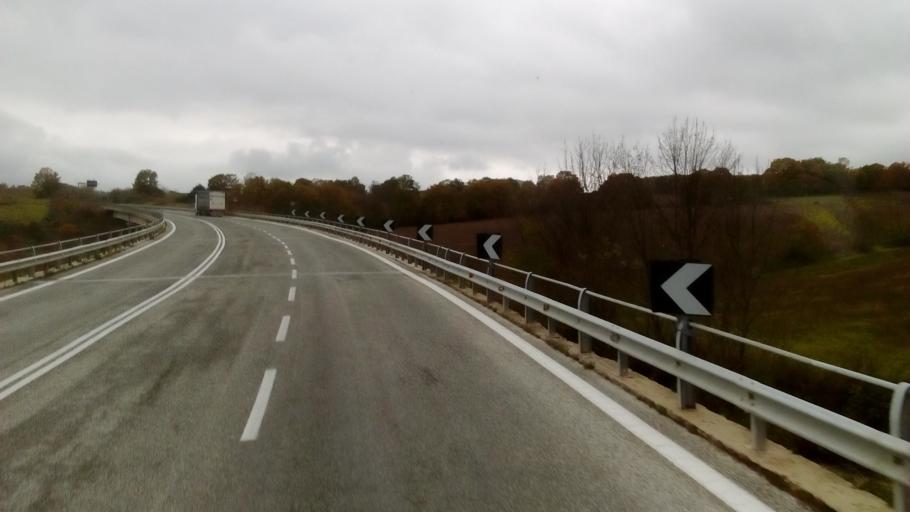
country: IT
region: Molise
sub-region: Provincia di Isernia
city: Bagnoli del Trigno
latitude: 41.7173
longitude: 14.4247
